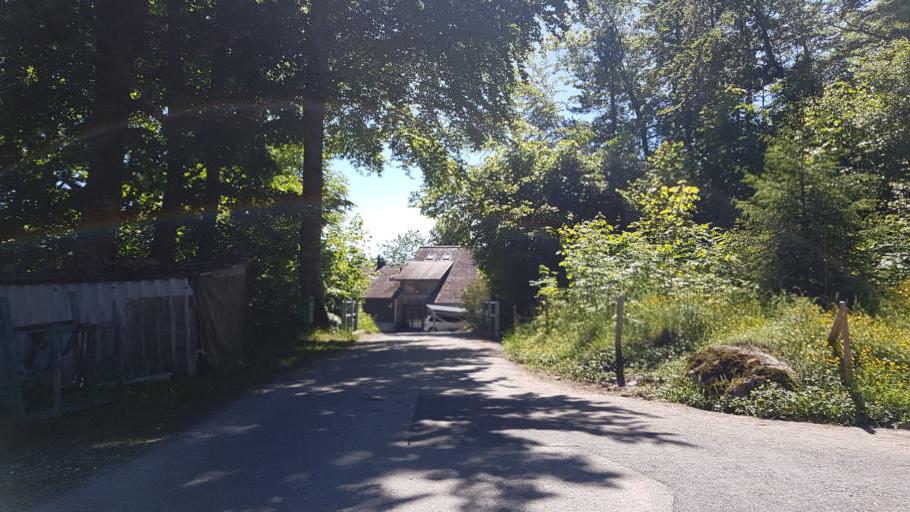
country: CH
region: Bern
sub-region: Thun District
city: Blumenstein
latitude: 46.7263
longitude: 7.5270
